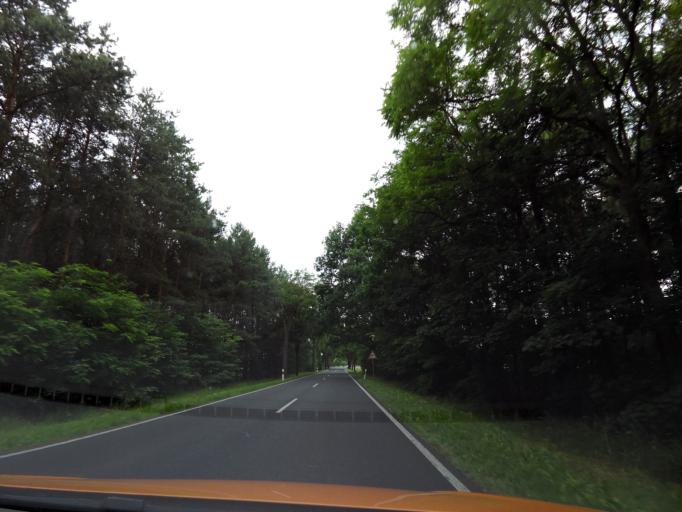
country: DE
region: Brandenburg
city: Baruth
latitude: 52.1296
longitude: 13.4783
